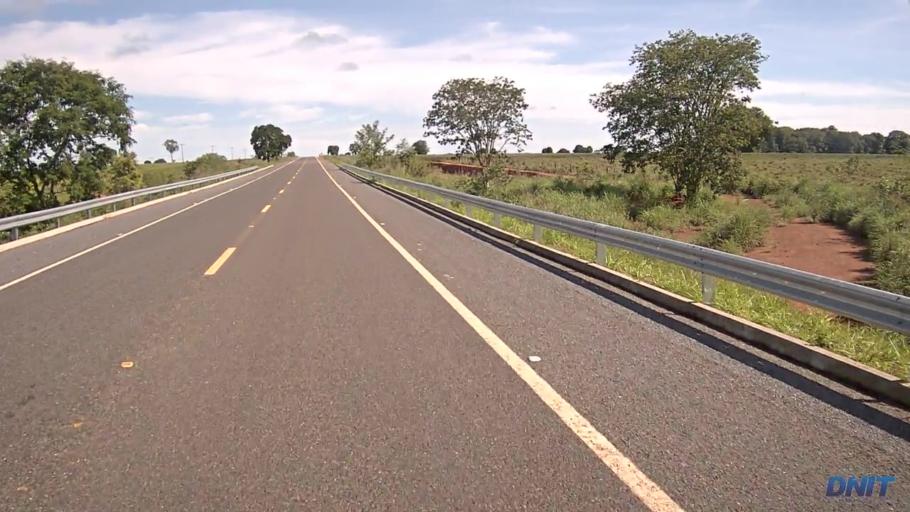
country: BR
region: Goias
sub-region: Sao Miguel Do Araguaia
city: Sao Miguel do Araguaia
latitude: -13.3783
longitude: -50.1415
